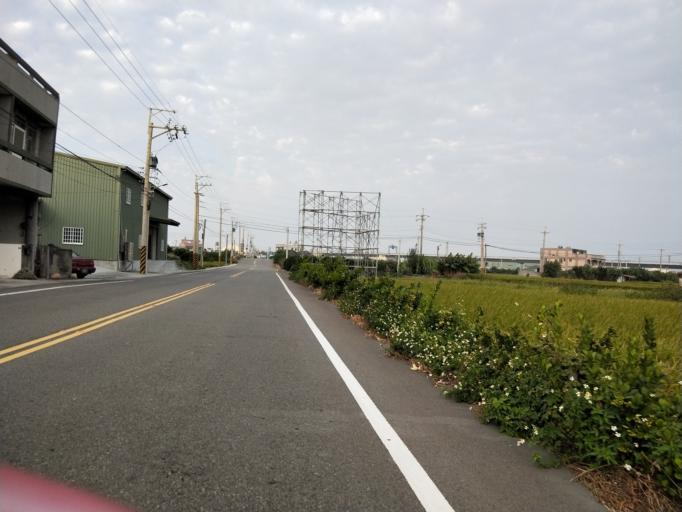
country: TW
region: Taiwan
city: Fengyuan
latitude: 24.3808
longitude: 120.5881
